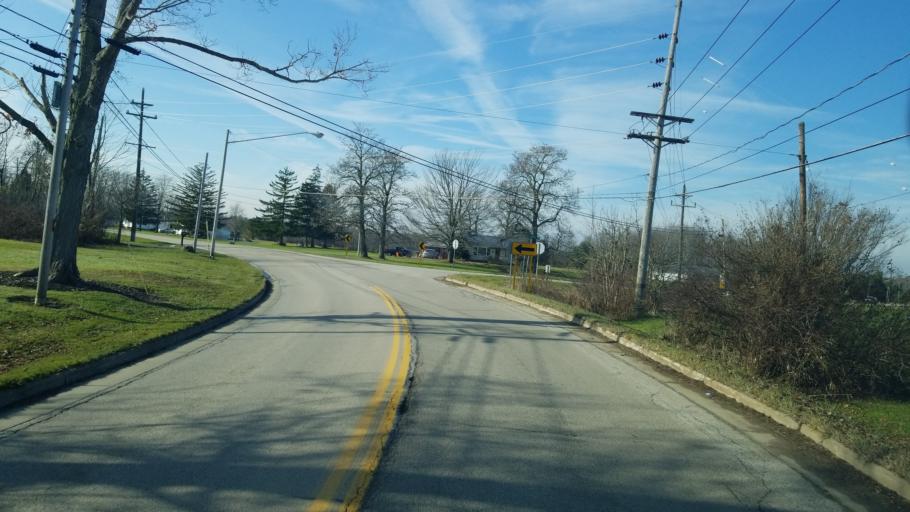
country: US
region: Ohio
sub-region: Ashtabula County
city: Jefferson
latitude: 41.7387
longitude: -80.7945
